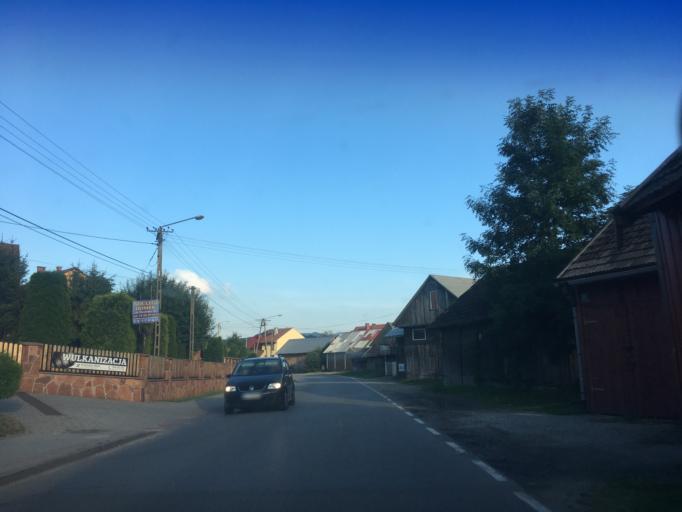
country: PL
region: Lesser Poland Voivodeship
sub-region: Powiat nowotarski
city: Kroscienko nad Dunajcem
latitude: 49.3950
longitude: 20.3843
